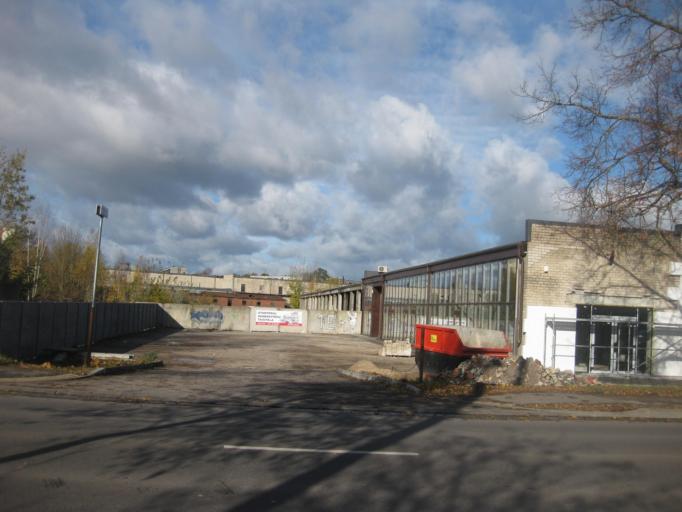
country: LT
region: Kauno apskritis
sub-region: Kaunas
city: Eiguliai
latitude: 54.9075
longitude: 23.9379
